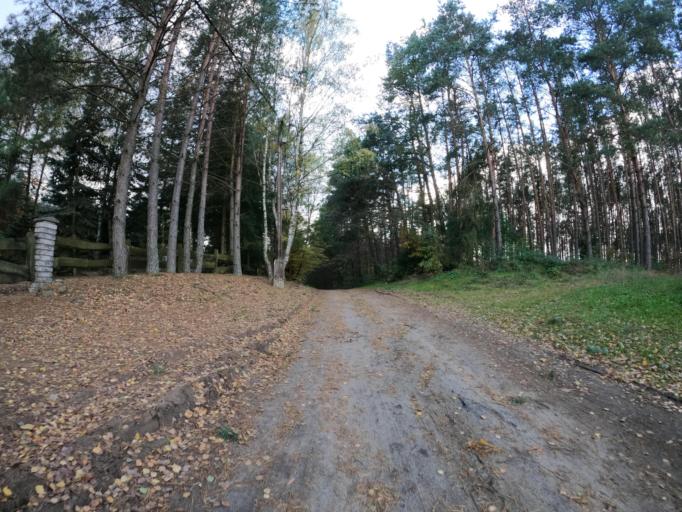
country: PL
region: West Pomeranian Voivodeship
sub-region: Powiat mysliborski
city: Barlinek
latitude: 52.9126
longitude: 15.2820
